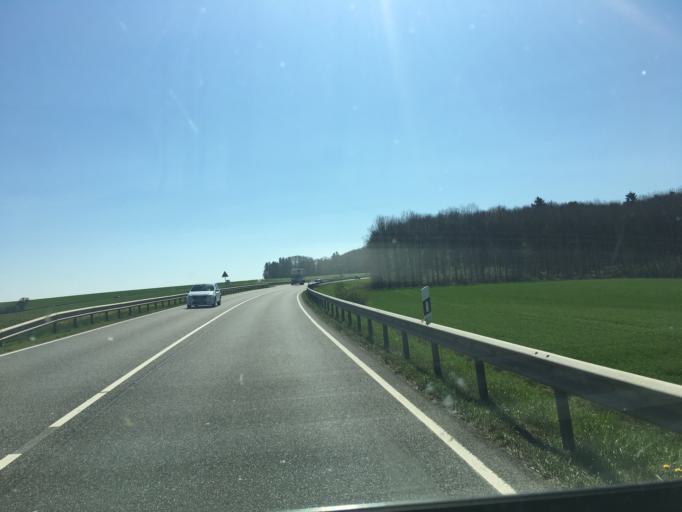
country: DE
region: Rheinland-Pfalz
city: Newel
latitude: 49.8268
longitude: 6.5670
